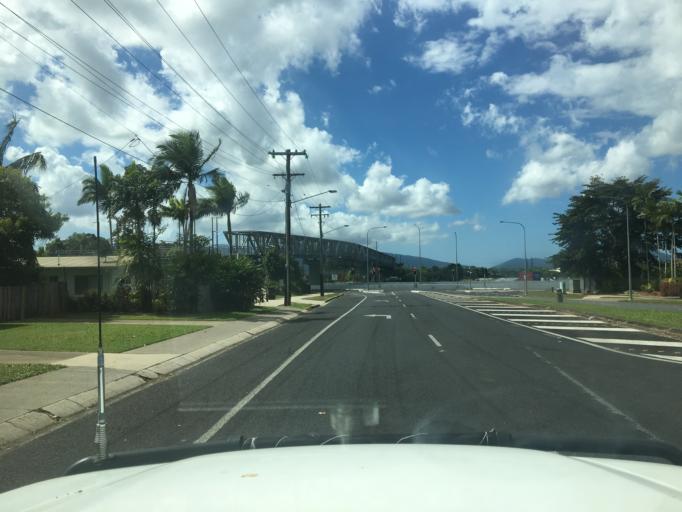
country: AU
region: Queensland
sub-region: Cairns
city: Woree
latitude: -16.9676
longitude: 145.7452
